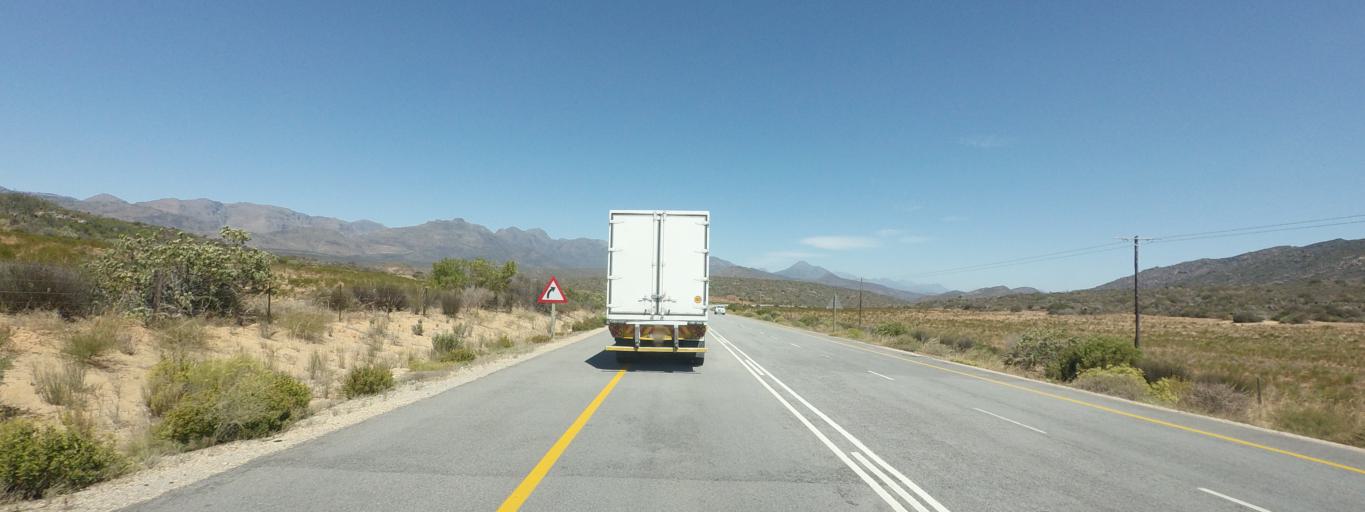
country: ZA
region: Western Cape
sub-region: West Coast District Municipality
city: Clanwilliam
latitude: -32.3250
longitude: 18.9197
